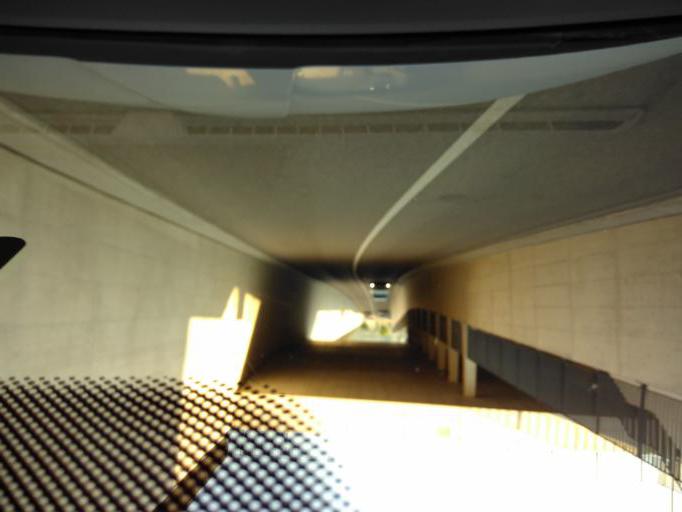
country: CH
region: Zurich
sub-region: Bezirk Dielsdorf
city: Regensdorf / Feldblumen-Riedthofstrasse
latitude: 47.4415
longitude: 8.4640
